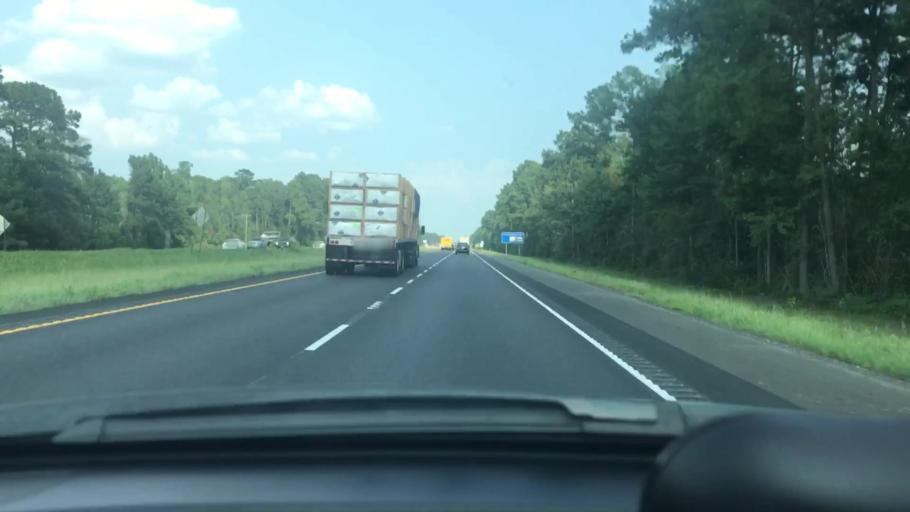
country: US
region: Louisiana
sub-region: Livingston Parish
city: Albany
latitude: 30.4745
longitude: -90.6617
